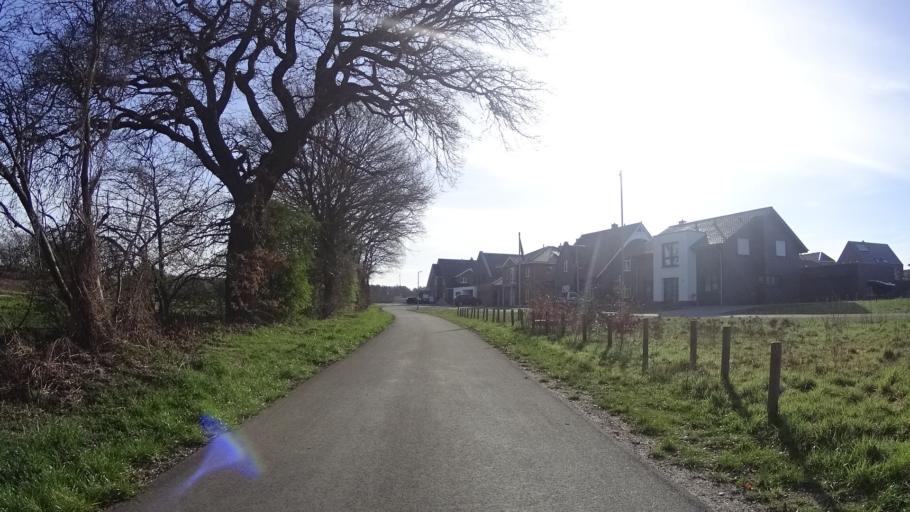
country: DE
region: Lower Saxony
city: Haren
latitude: 52.7977
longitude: 7.2641
